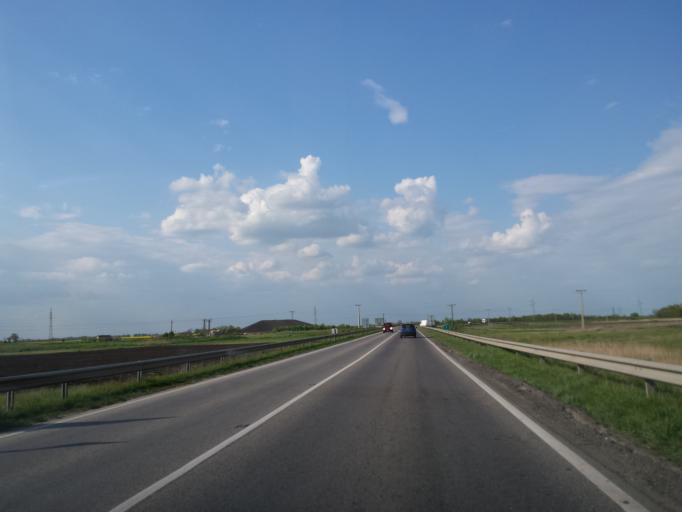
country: HU
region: Csongrad
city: Mako
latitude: 46.2440
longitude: 20.4816
